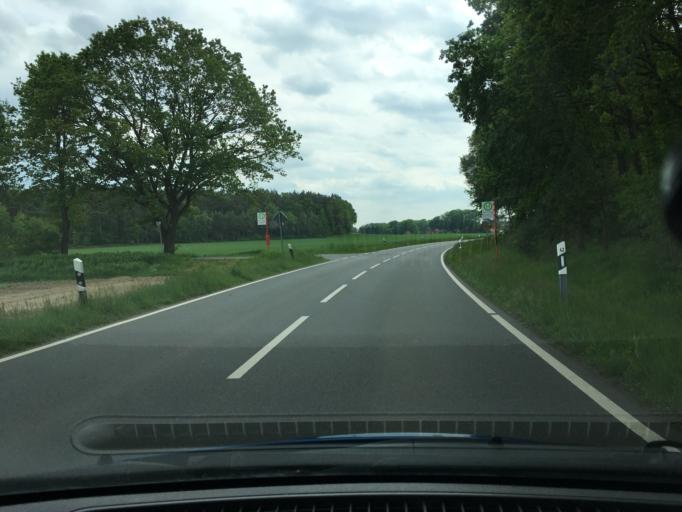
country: DE
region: Lower Saxony
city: Betzendorf
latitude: 53.1193
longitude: 10.3084
